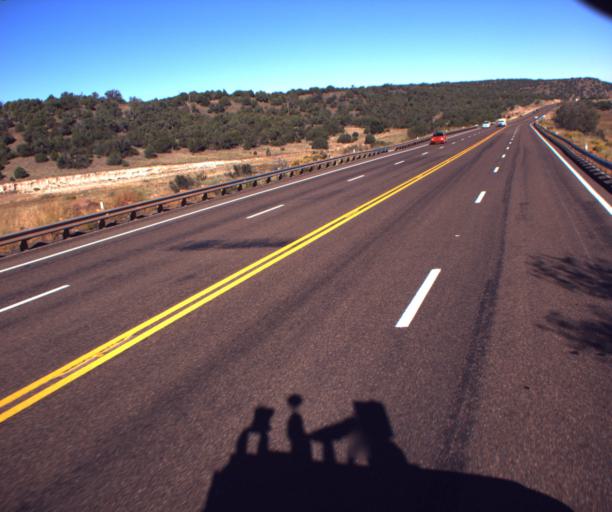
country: US
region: Arizona
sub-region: Navajo County
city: White Mountain Lake
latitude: 34.3758
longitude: -110.0536
